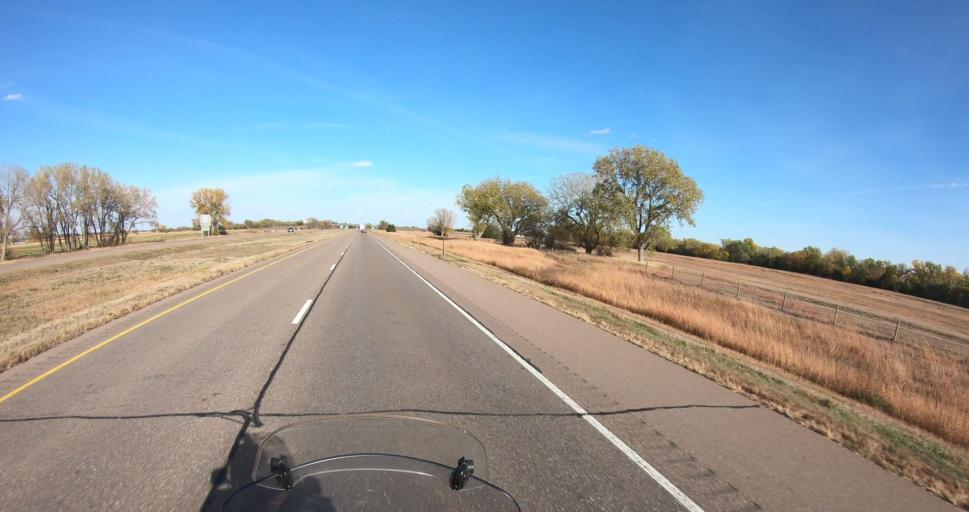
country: US
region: Nebraska
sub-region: Buffalo County
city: Gibbon
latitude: 40.7077
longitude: -98.8244
